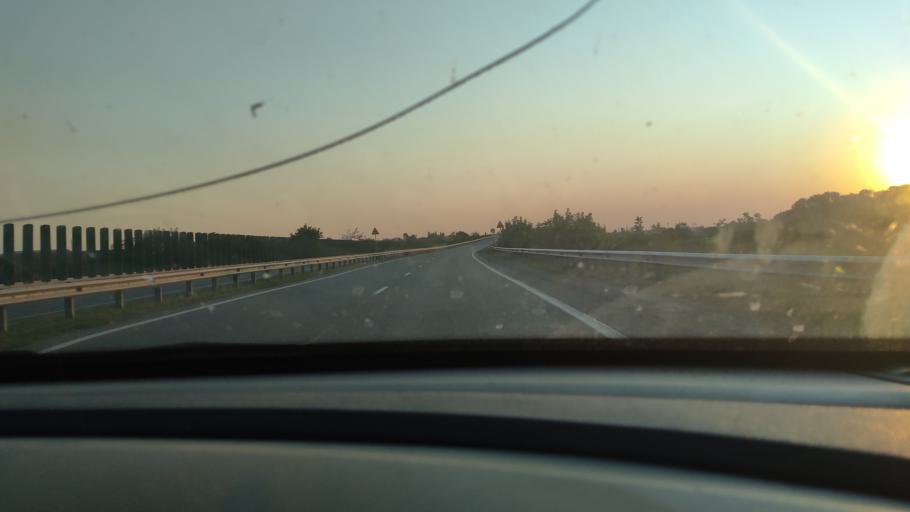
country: RU
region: Krasnodarskiy
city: Timashevsk
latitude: 45.6037
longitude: 38.9782
